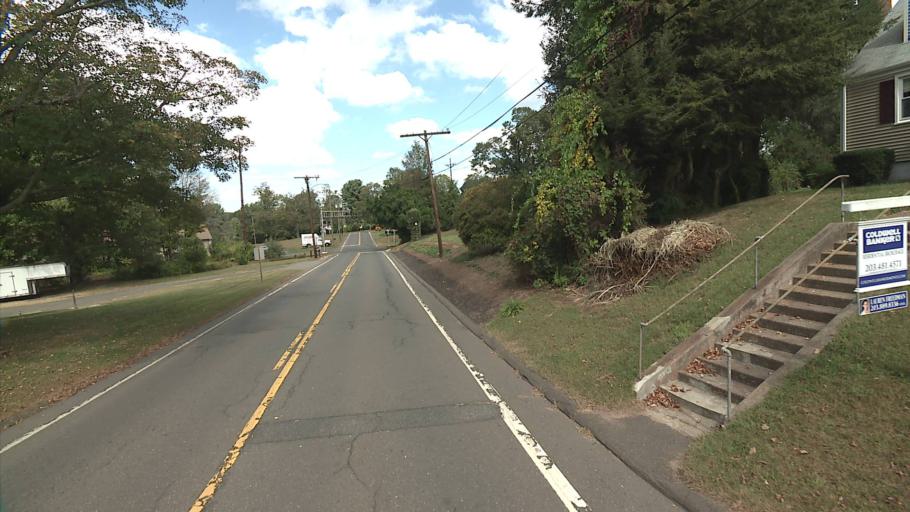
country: US
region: Connecticut
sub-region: Middlesex County
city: Middletown
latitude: 41.5431
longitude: -72.6825
